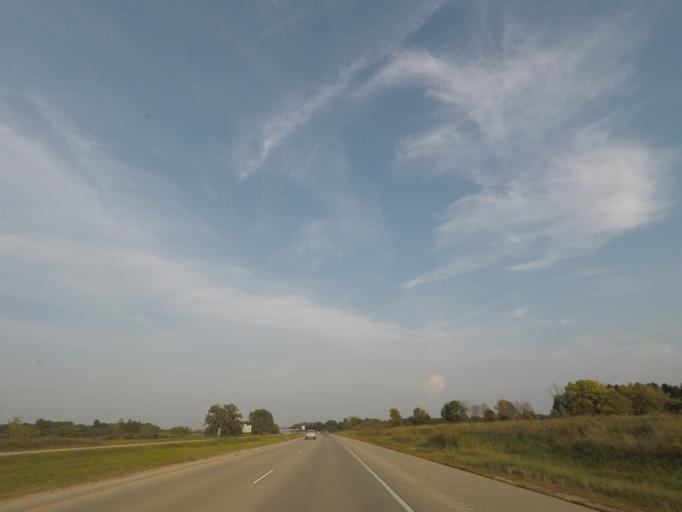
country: US
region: Wisconsin
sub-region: Dane County
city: Cottage Grove
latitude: 43.1091
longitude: -89.1772
